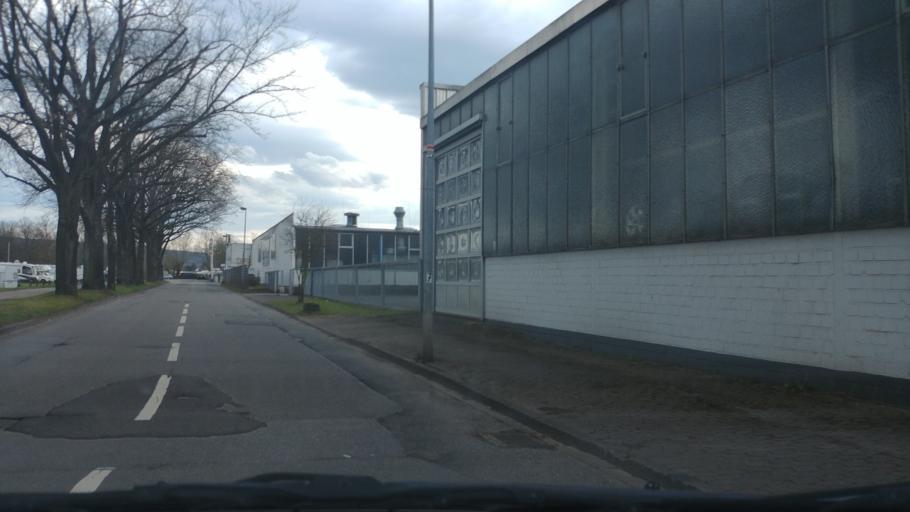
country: DE
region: Lower Saxony
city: Holzminden
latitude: 51.8291
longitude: 9.4386
